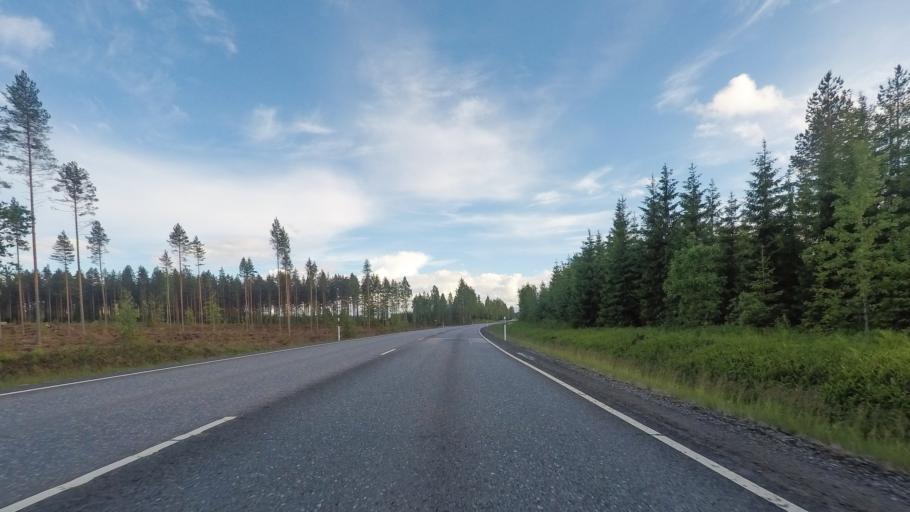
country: FI
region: Central Finland
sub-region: Joutsa
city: Joutsa
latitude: 61.6923
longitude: 26.0590
